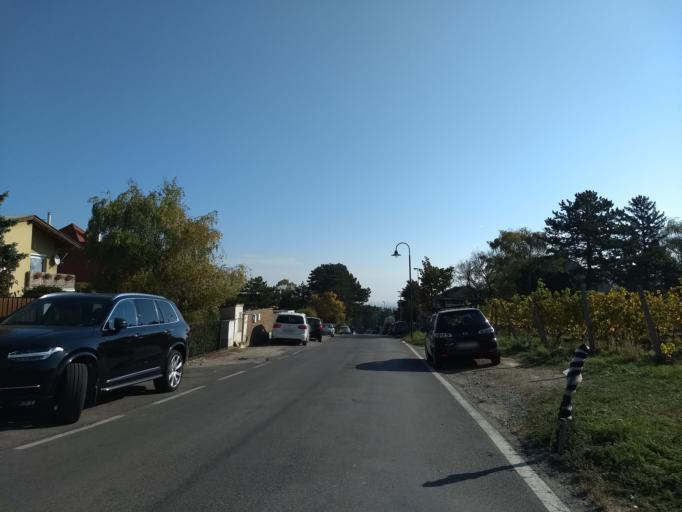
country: AT
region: Lower Austria
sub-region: Politischer Bezirk Modling
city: Perchtoldsdorf
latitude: 48.1126
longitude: 16.2648
